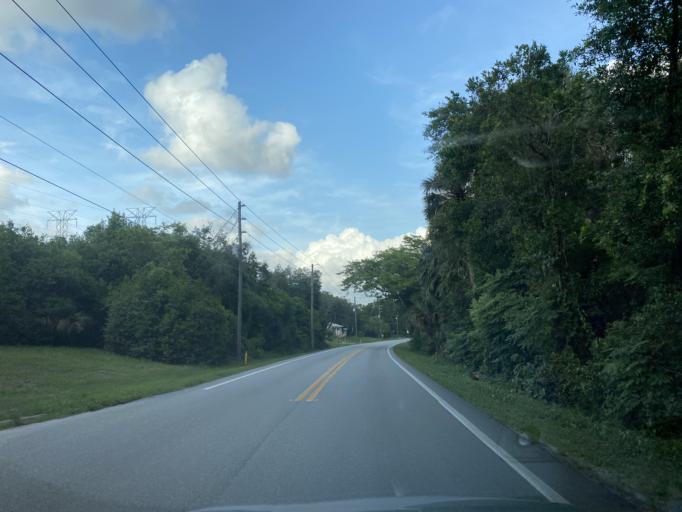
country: US
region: Florida
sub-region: Volusia County
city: DeBary
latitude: 28.8682
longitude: -81.3088
